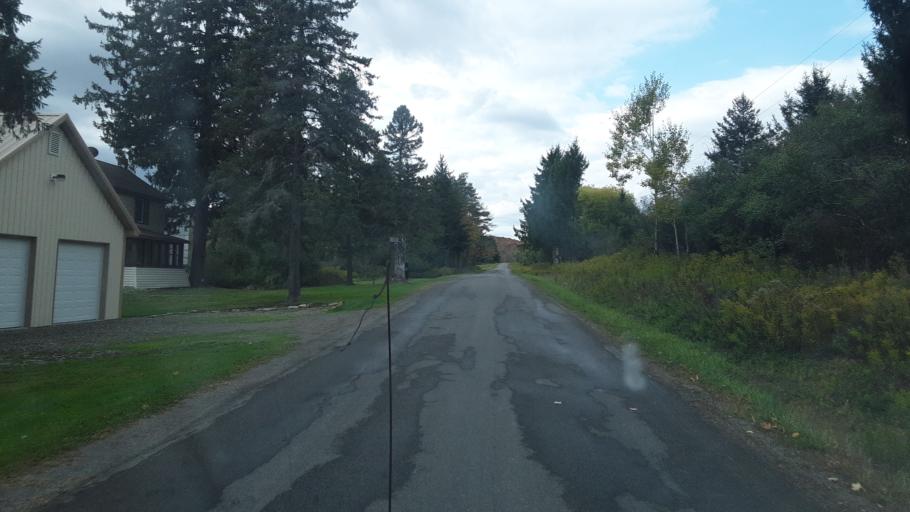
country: US
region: New York
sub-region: Allegany County
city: Alfred
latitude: 42.3645
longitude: -77.8244
